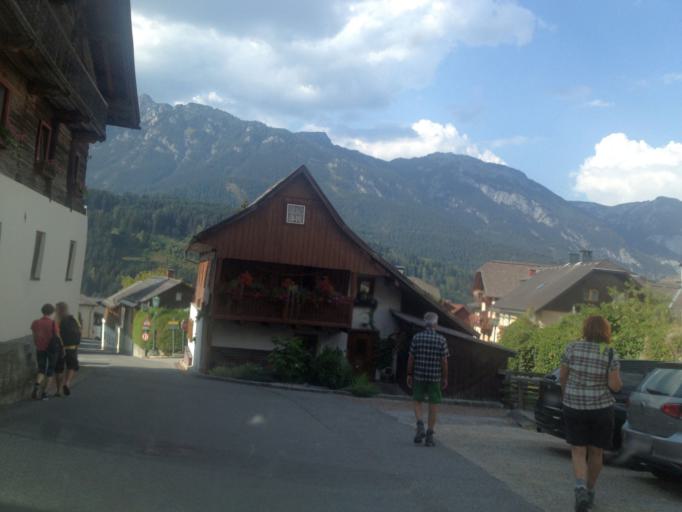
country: AT
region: Styria
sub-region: Politischer Bezirk Liezen
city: Haus
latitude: 47.4092
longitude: 13.7670
